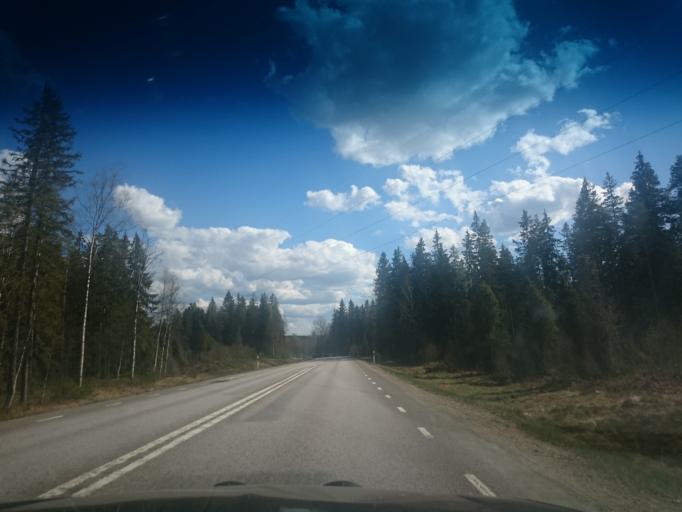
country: SE
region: Kronoberg
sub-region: Vaxjo Kommun
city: Braas
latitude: 57.2405
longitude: 15.1424
